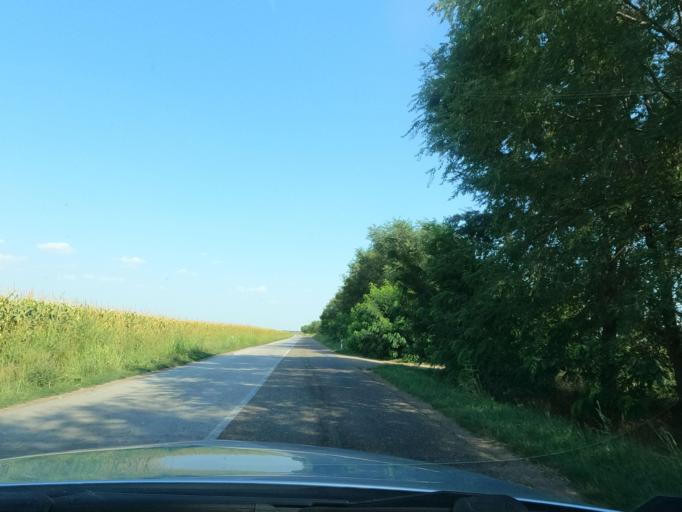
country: RS
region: Autonomna Pokrajina Vojvodina
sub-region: Juznobacki Okrug
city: Becej
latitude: 45.6529
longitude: 19.9678
